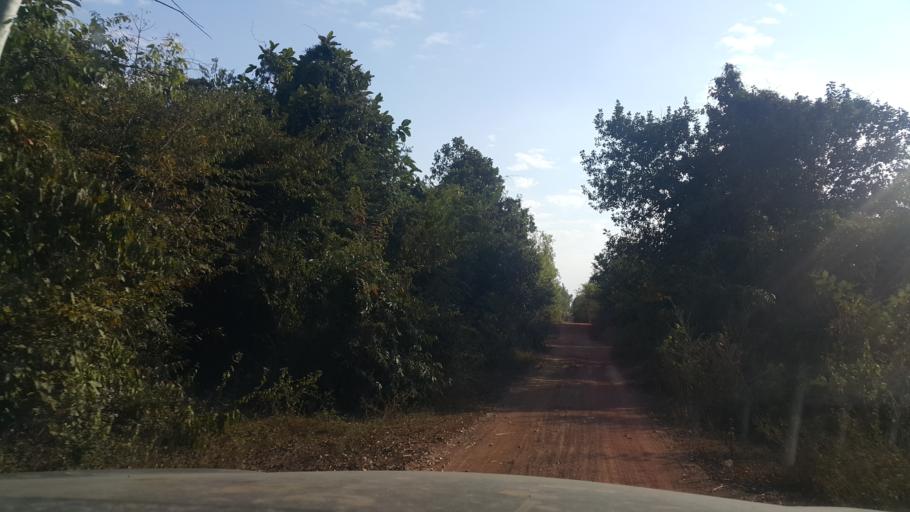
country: TH
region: Lampang
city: Hang Chat
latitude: 18.2842
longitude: 99.3576
